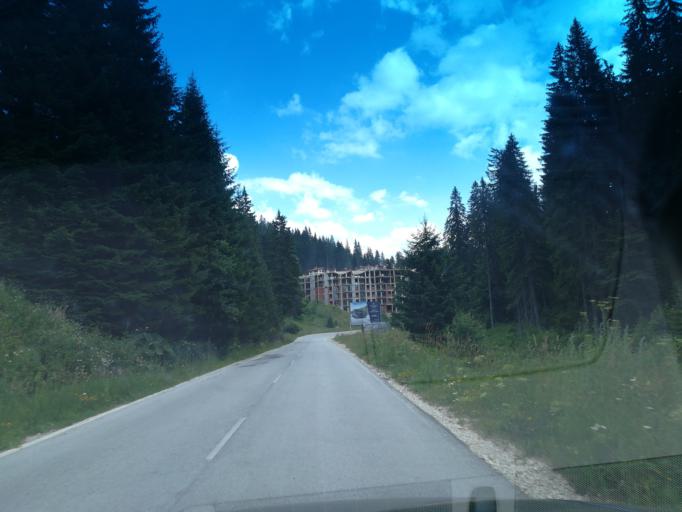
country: BG
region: Smolyan
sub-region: Obshtina Smolyan
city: Smolyan
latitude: 41.6560
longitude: 24.6863
